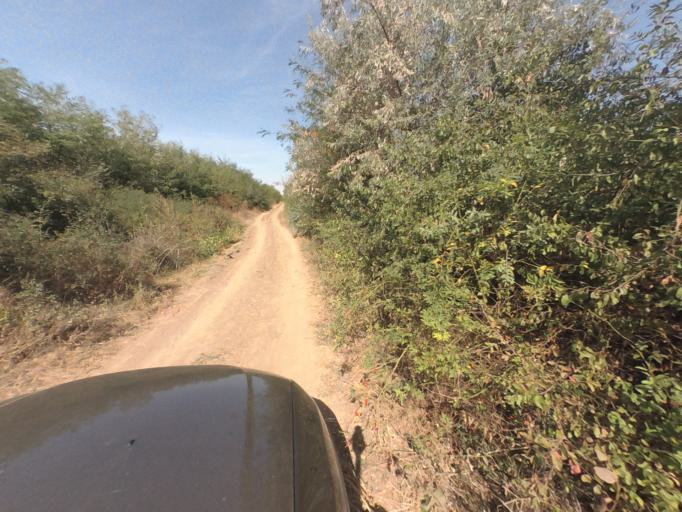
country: RO
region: Vaslui
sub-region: Comuna Costesti
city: Costesti
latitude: 46.5181
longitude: 27.7416
